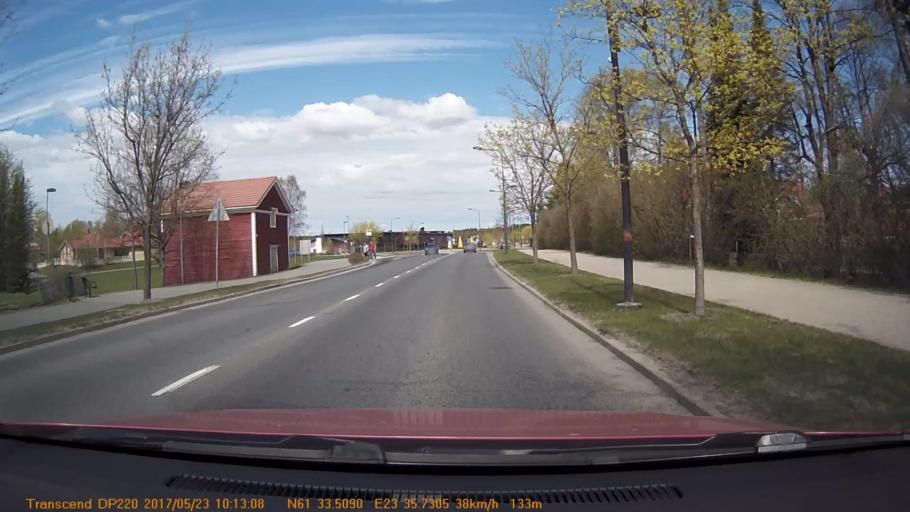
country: FI
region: Pirkanmaa
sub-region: Tampere
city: Yloejaervi
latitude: 61.5583
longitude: 23.5956
